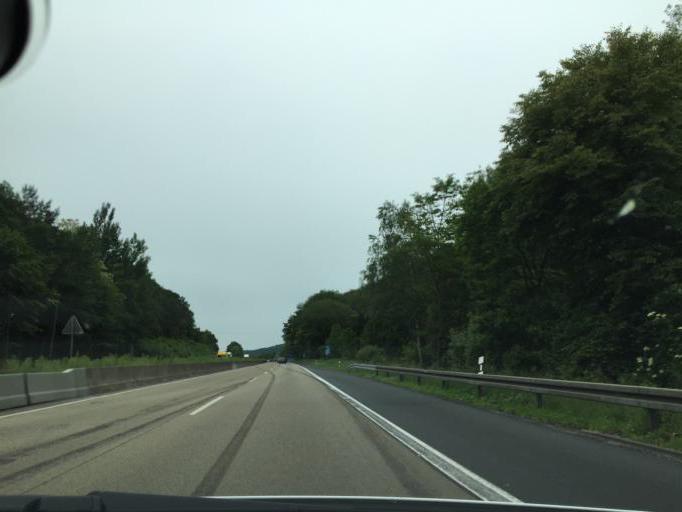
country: DE
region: Bavaria
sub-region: Regierungsbezirk Unterfranken
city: Motten
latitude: 50.4260
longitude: 9.7403
